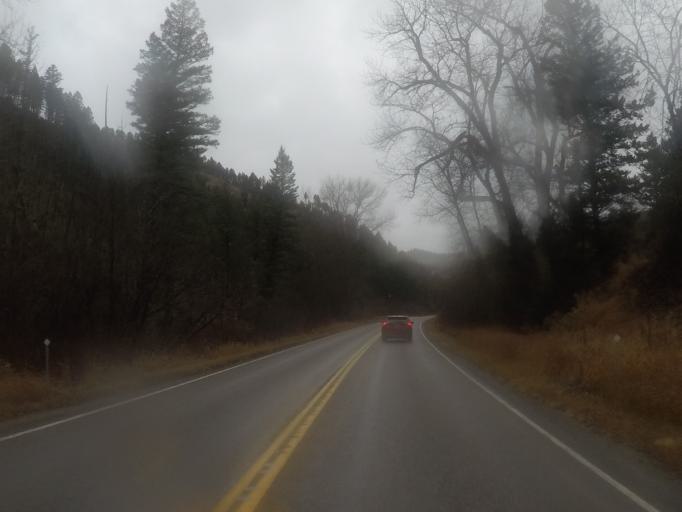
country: US
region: Montana
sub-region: Broadwater County
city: Townsend
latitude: 46.3300
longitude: -111.2061
